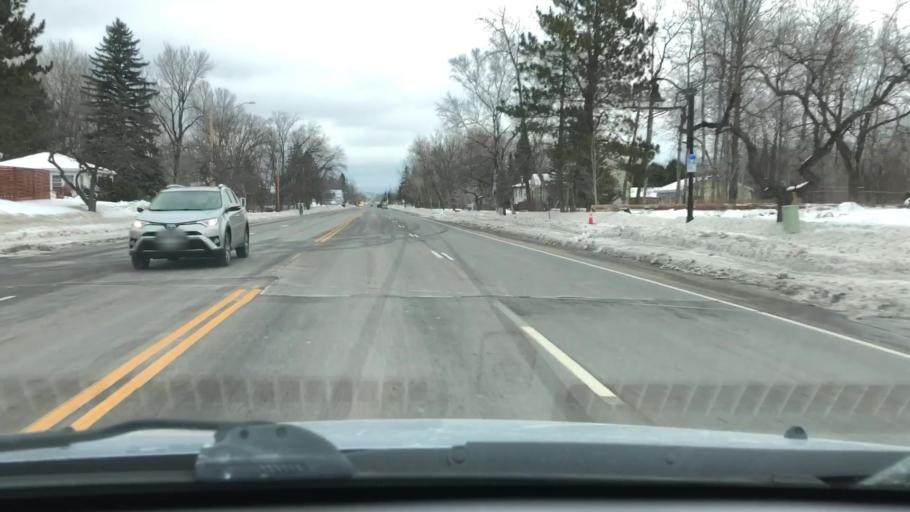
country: US
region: Minnesota
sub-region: Saint Louis County
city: Proctor
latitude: 46.7187
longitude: -92.1979
